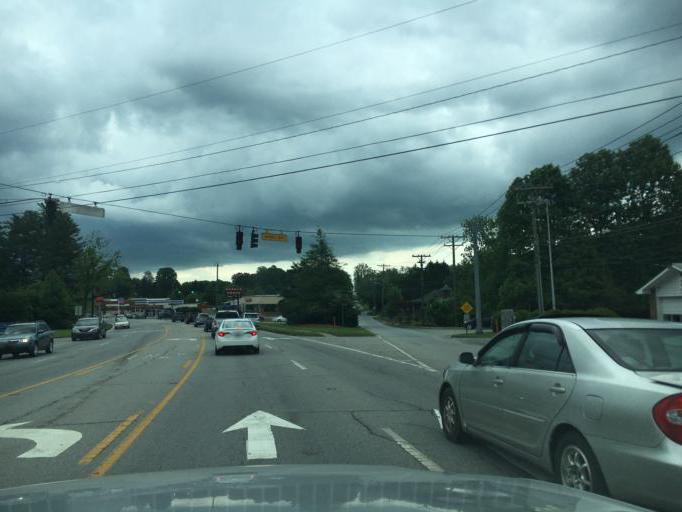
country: US
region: North Carolina
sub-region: Transylvania County
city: Brevard
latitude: 35.2422
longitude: -82.7259
